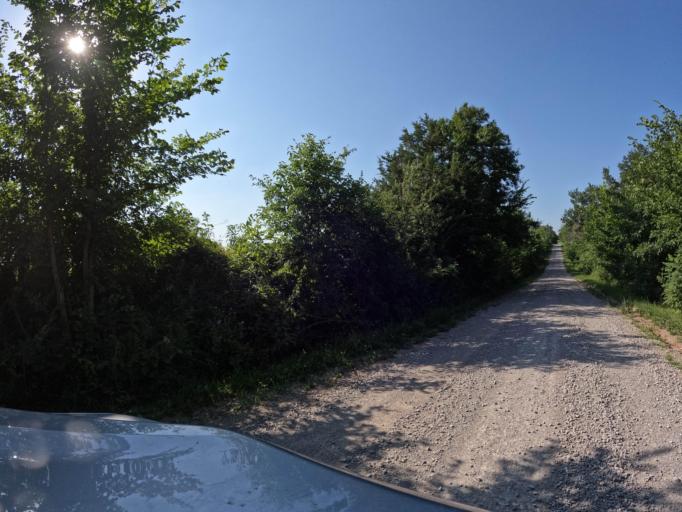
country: US
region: Iowa
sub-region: Appanoose County
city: Centerville
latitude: 40.7364
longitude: -93.0207
